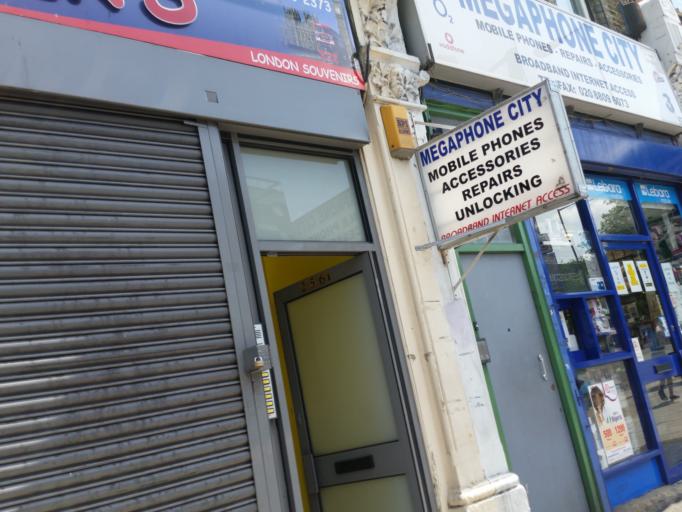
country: GB
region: England
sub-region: Greater London
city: Harringay
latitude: 51.5744
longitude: -0.0722
